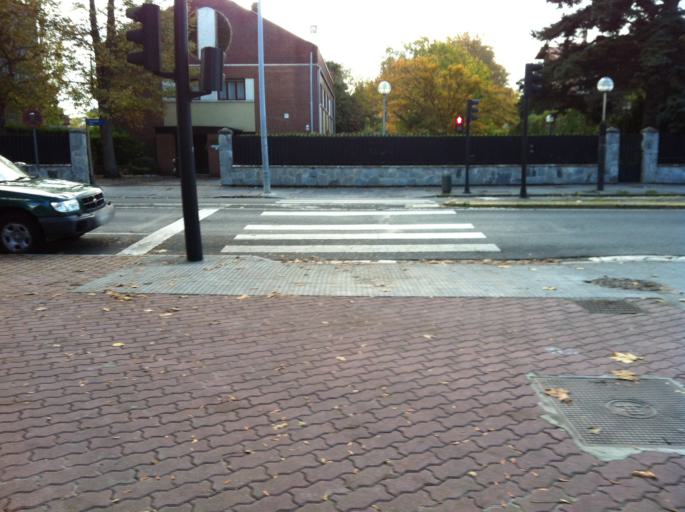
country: ES
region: Basque Country
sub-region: Provincia de Alava
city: Gasteiz / Vitoria
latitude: 42.8372
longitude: -2.6753
